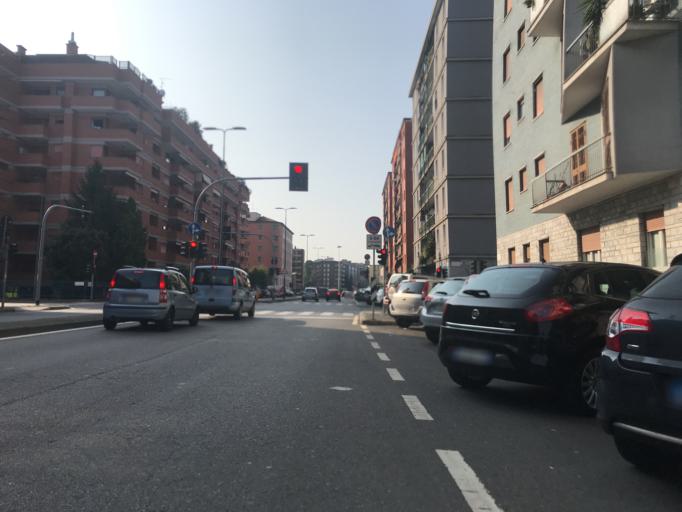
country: IT
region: Lombardy
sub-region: Citta metropolitana di Milano
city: Sesto San Giovanni
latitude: 45.4941
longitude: 9.2359
